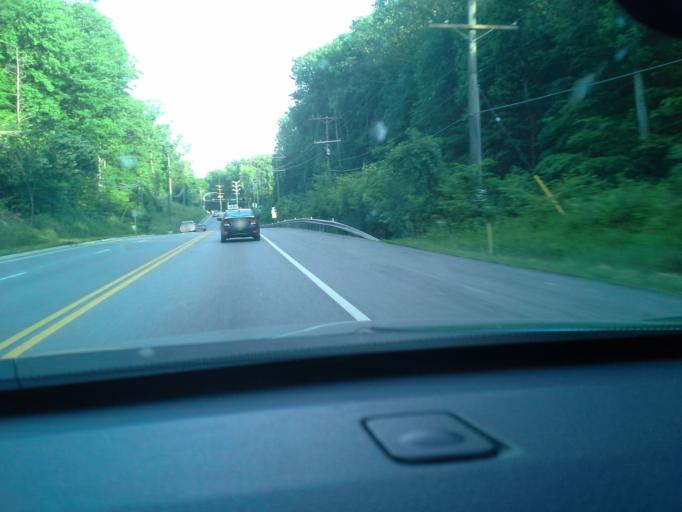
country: US
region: Maryland
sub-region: Anne Arundel County
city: Londontowne
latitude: 38.9173
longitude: -76.5522
